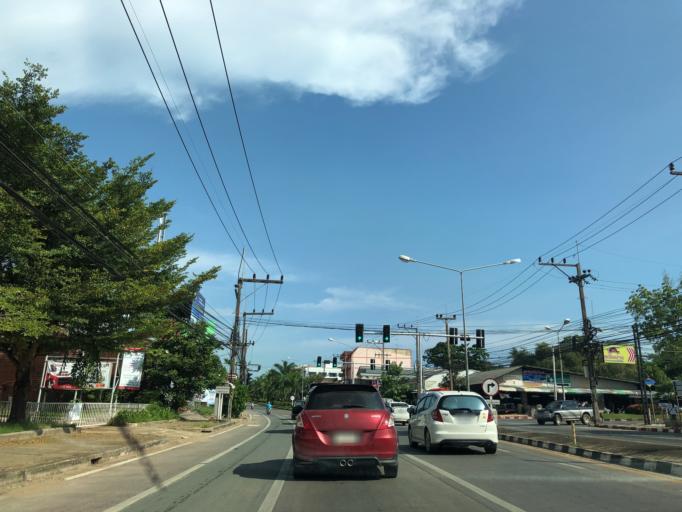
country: TH
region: Krabi
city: Krabi
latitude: 8.0864
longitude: 98.9131
